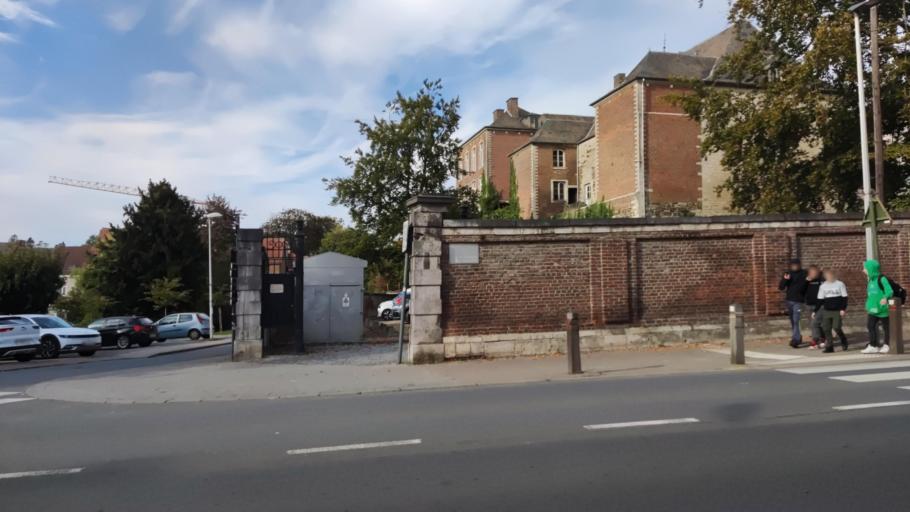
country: BE
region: Wallonia
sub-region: Province du Brabant Wallon
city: Jodoigne
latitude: 50.7237
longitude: 4.8670
